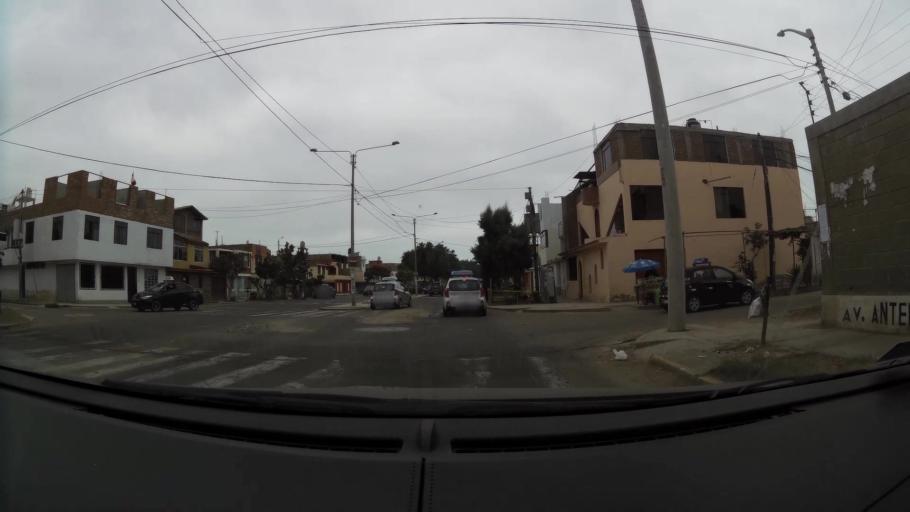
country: PE
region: La Libertad
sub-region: Provincia de Trujillo
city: Trujillo
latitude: -8.1106
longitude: -79.0399
